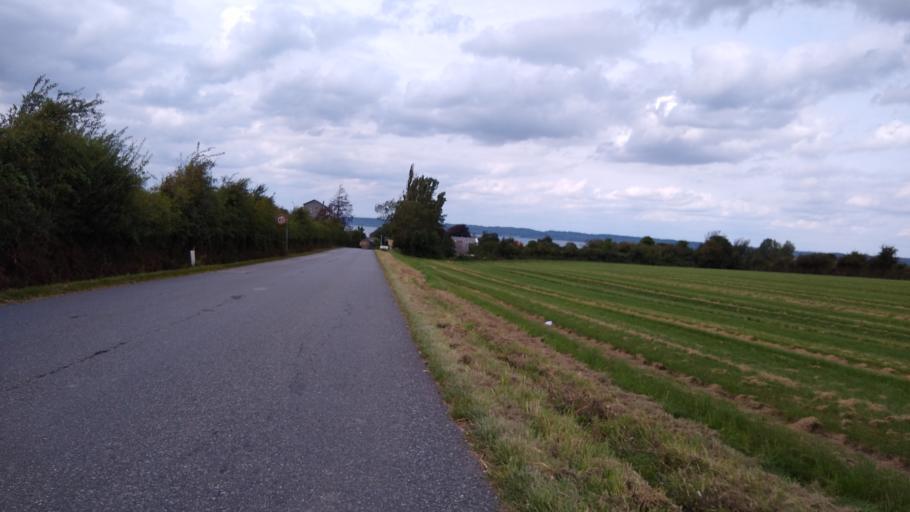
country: DK
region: South Denmark
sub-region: Fredericia Kommune
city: Fredericia
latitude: 55.6163
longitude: 9.7771
